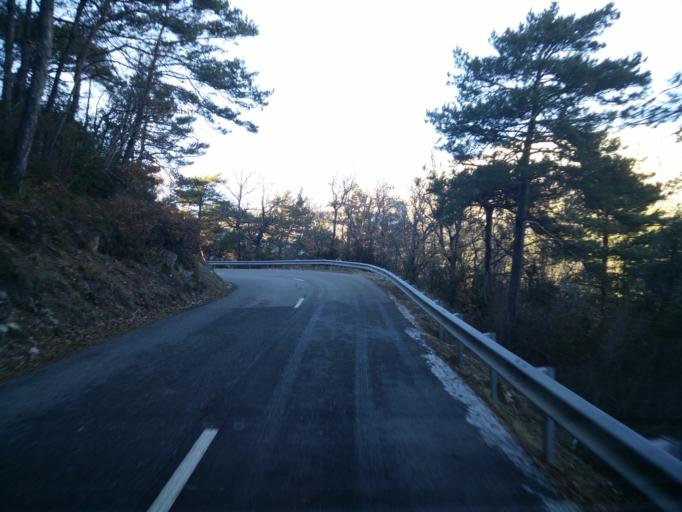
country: FR
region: Provence-Alpes-Cote d'Azur
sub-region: Departement des Alpes-de-Haute-Provence
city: Castellane
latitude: 43.7896
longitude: 6.3777
